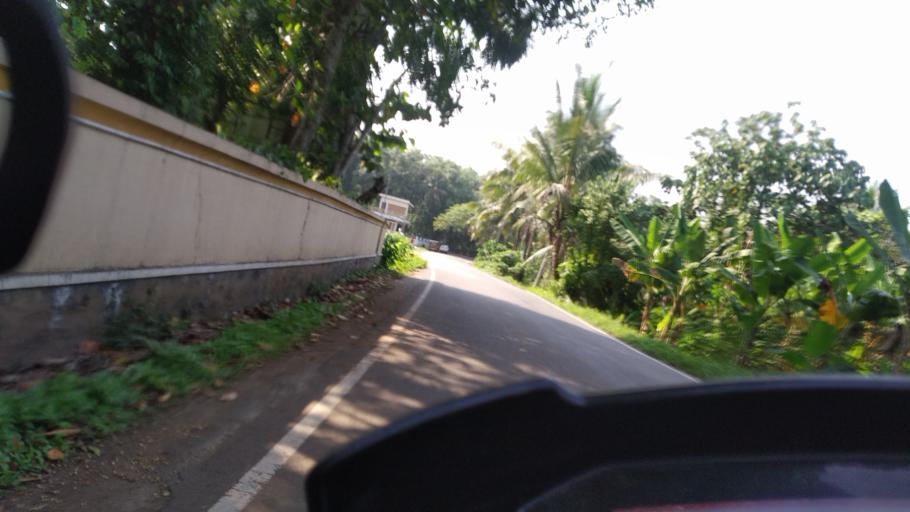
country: IN
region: Kerala
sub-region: Ernakulam
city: Piravam
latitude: 9.8386
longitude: 76.5361
